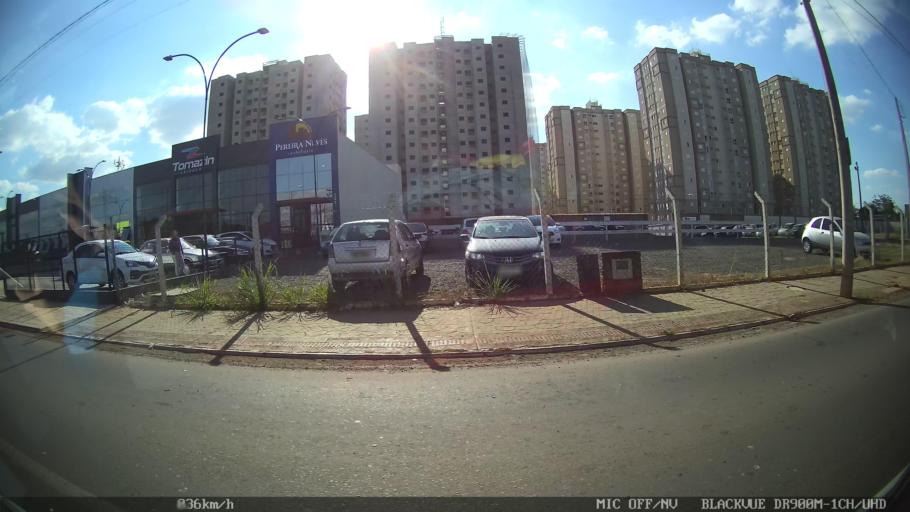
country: BR
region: Sao Paulo
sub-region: Nova Odessa
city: Nova Odessa
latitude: -22.7896
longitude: -47.3049
